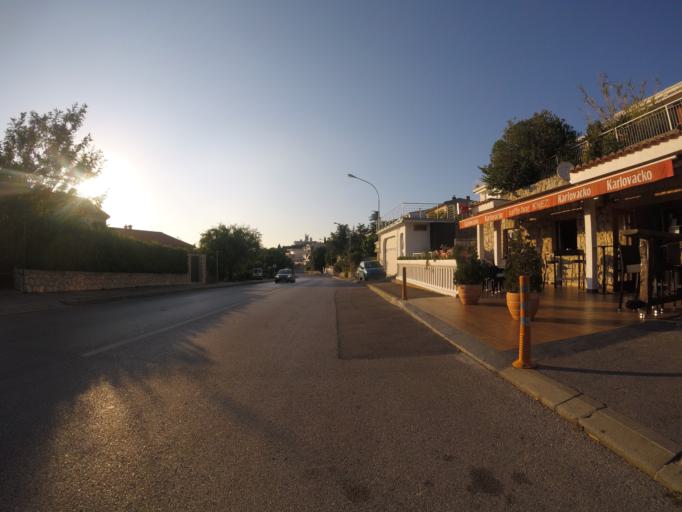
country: HR
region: Primorsko-Goranska
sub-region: Grad Crikvenica
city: Crikvenica
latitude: 45.1855
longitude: 14.6789
